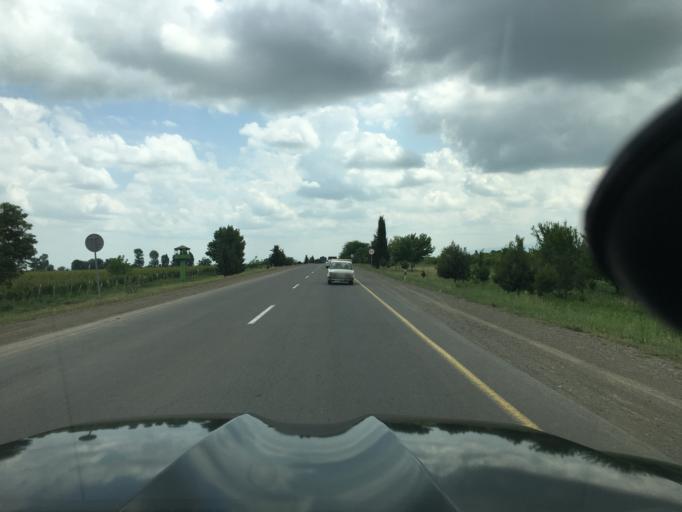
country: AZ
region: Tovuz
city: Tovuz
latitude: 40.9682
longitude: 45.6971
